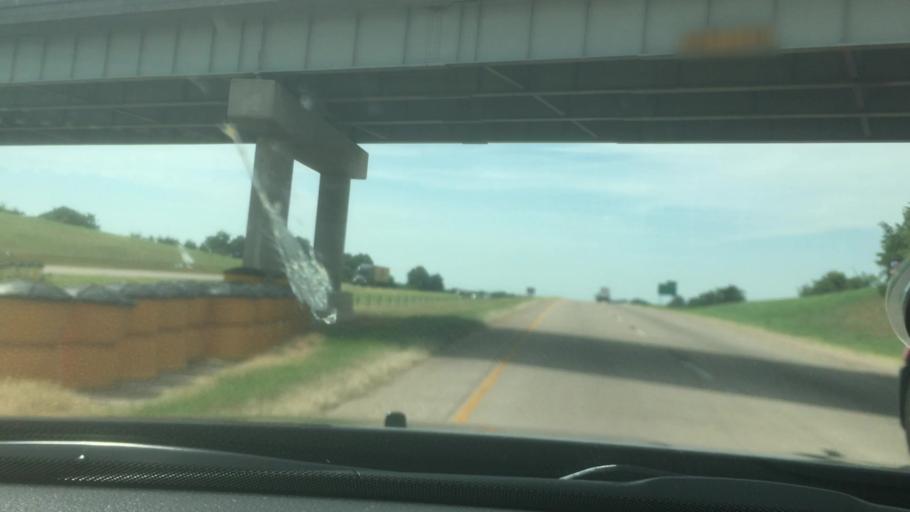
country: US
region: Oklahoma
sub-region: Garvin County
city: Pauls Valley
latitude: 34.7249
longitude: -97.2542
